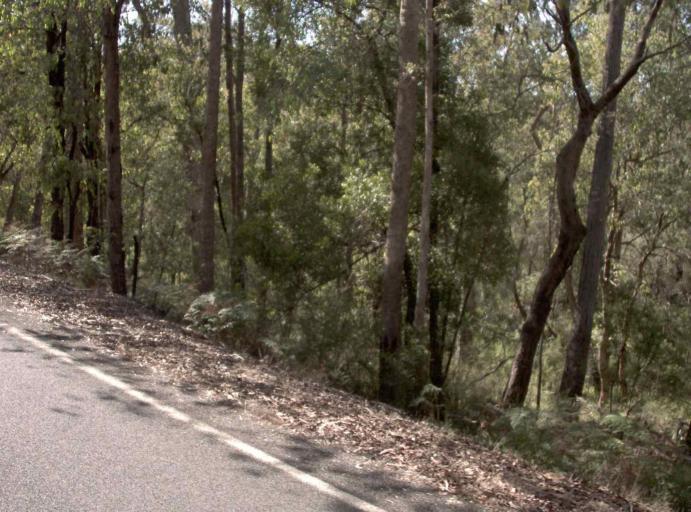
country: AU
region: New South Wales
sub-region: Bombala
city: Bombala
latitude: -37.3793
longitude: 148.6610
